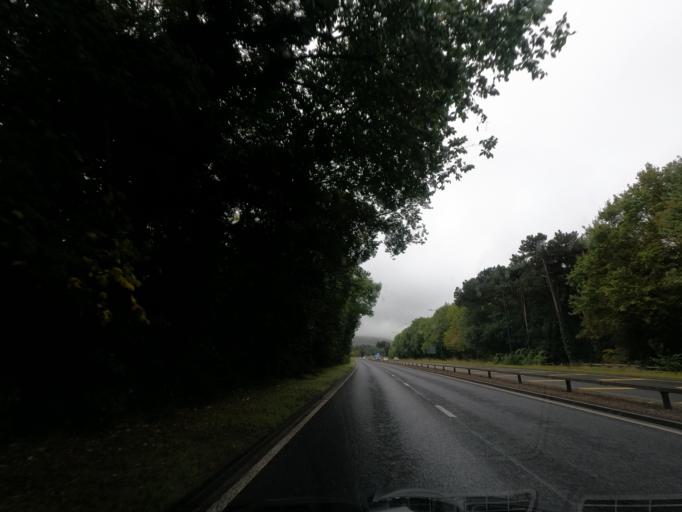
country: GB
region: England
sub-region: Redcar and Cleveland
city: Redcar
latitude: 54.5807
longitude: -1.0907
